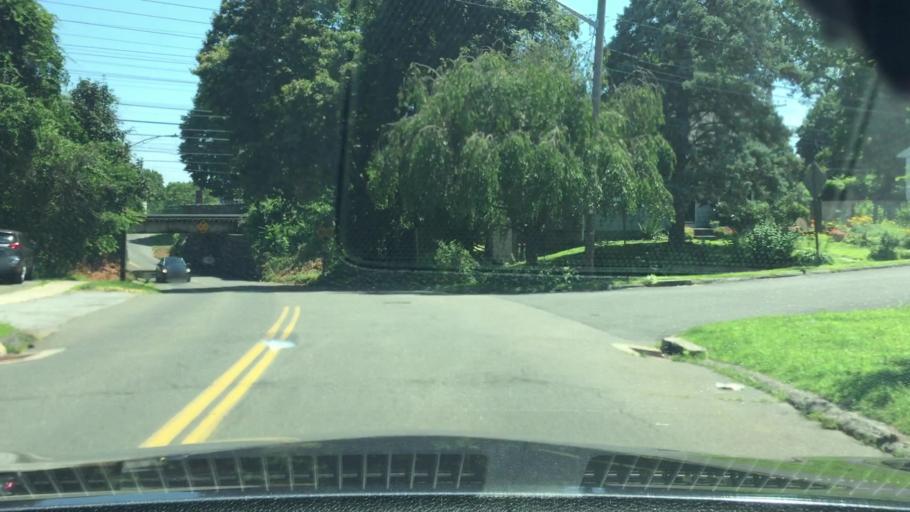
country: US
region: Connecticut
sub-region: New Haven County
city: City of Milford (balance)
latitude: 41.2199
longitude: -73.0655
